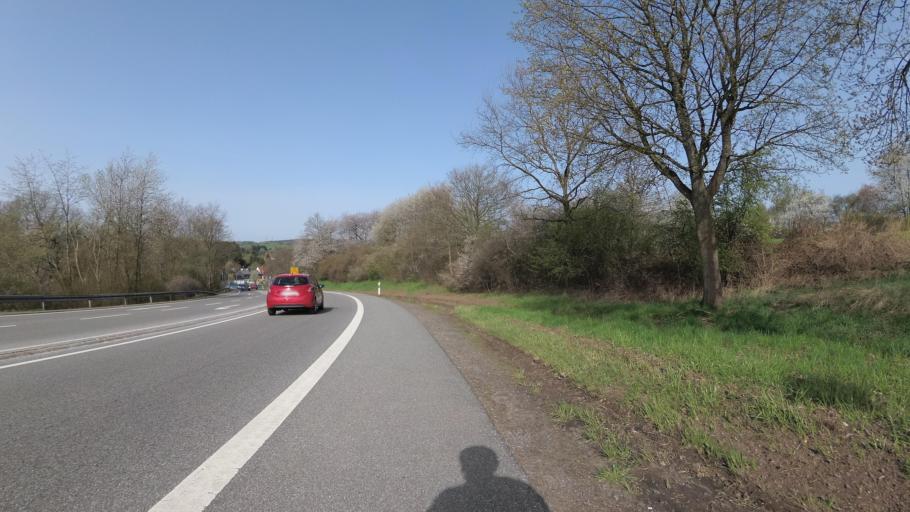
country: DE
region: Saarland
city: Illingen
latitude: 49.3828
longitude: 7.0518
